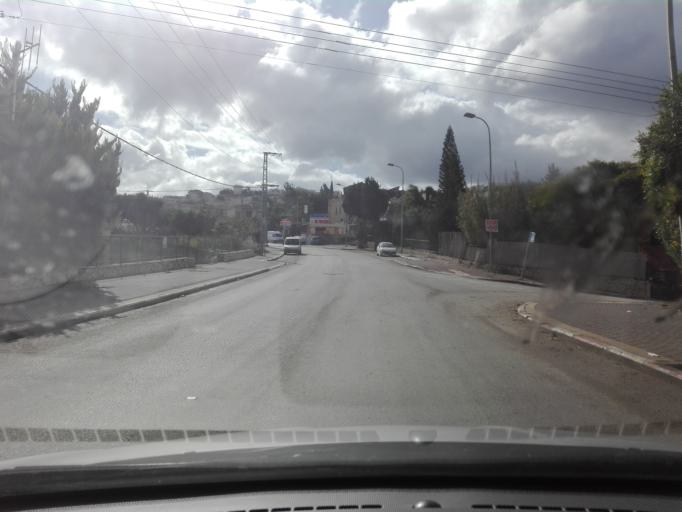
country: IL
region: Haifa
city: Daliyat el Karmil
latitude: 32.6949
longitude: 35.0633
